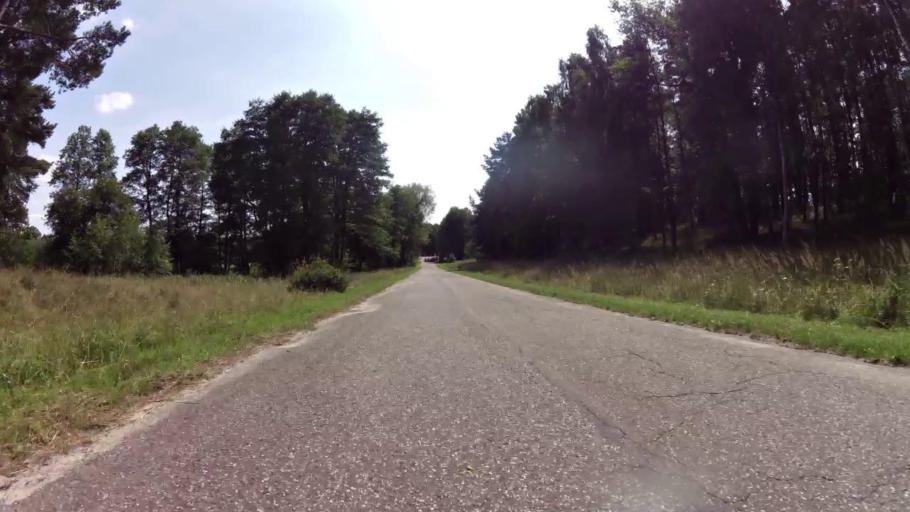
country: PL
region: West Pomeranian Voivodeship
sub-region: Powiat choszczenski
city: Drawno
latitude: 53.3193
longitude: 15.6873
